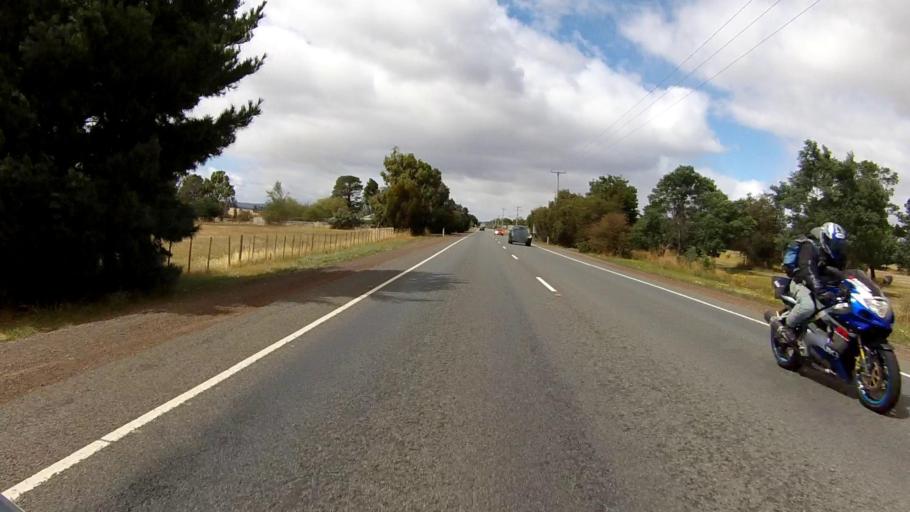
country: AU
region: Tasmania
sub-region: Northern Midlands
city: Evandale
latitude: -41.9424
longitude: 147.4919
